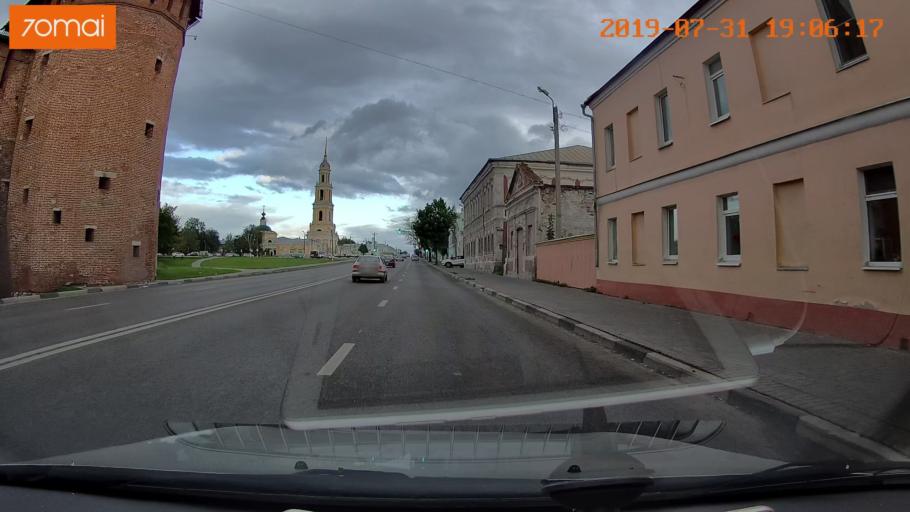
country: RU
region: Moskovskaya
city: Kolomna
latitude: 55.1031
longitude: 38.7516
